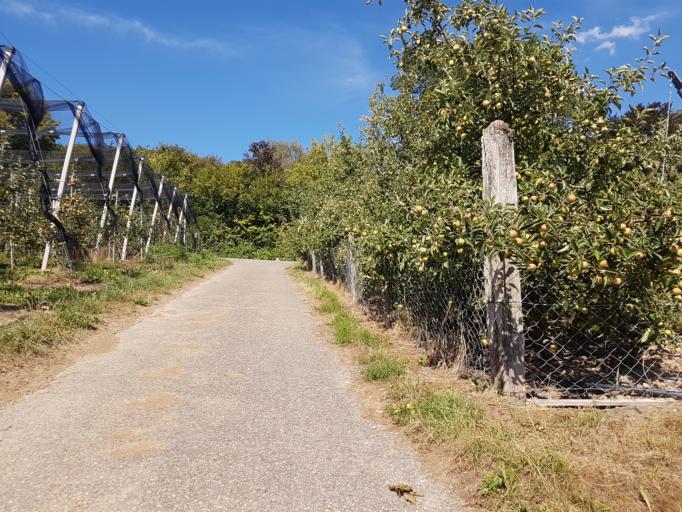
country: CH
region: Zurich
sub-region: Bezirk Pfaeffikon
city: Tagelswangen
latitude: 47.4232
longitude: 8.6778
